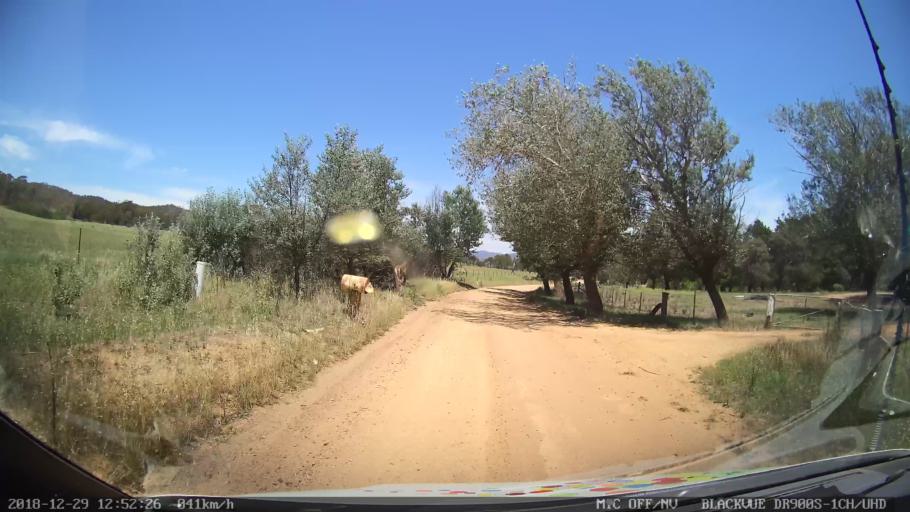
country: AU
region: Australian Capital Territory
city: Macarthur
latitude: -35.6808
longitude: 149.1941
